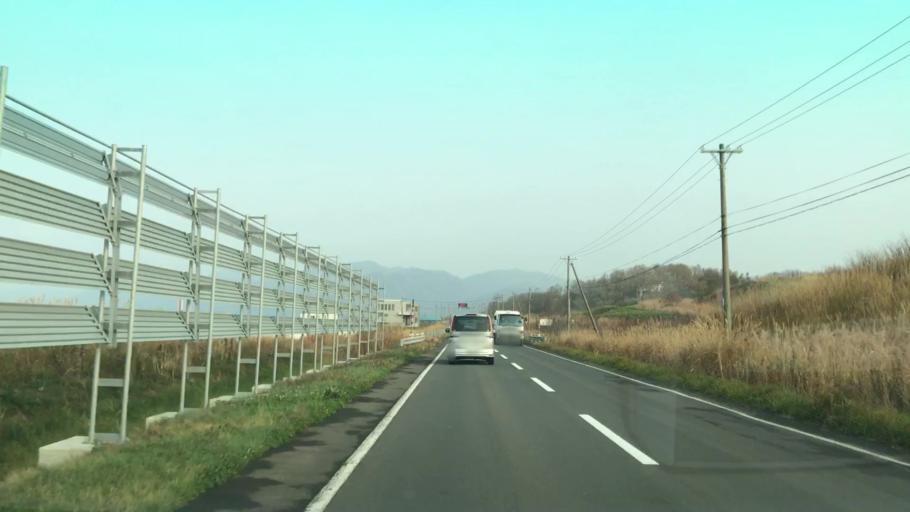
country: JP
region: Hokkaido
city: Ishikari
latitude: 43.3736
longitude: 141.4272
